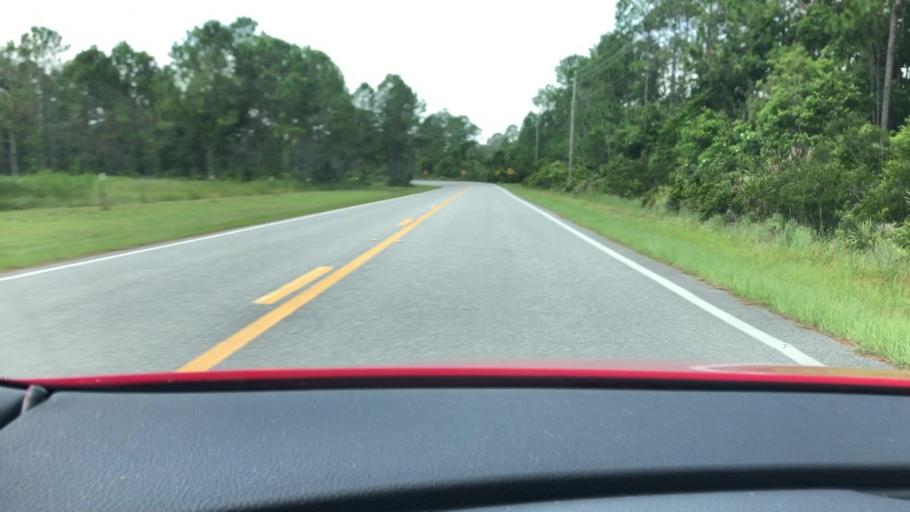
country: US
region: Florida
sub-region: Volusia County
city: Samsula-Spruce Creek
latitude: 29.0292
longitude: -81.0951
